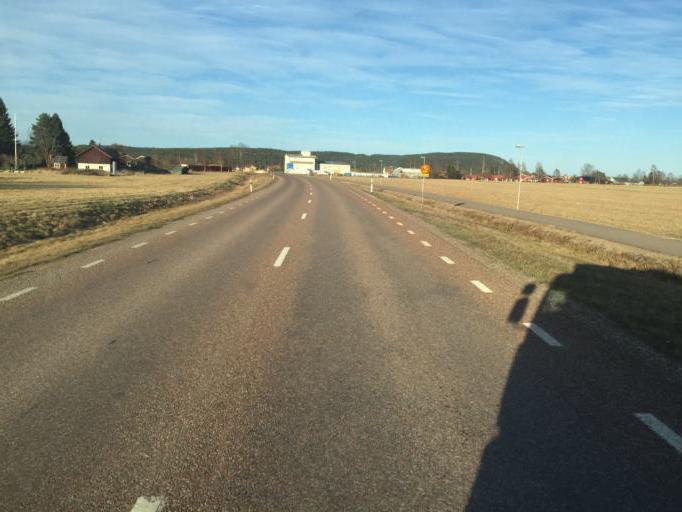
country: SE
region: Dalarna
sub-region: Gagnefs Kommun
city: Djuras
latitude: 60.5547
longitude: 15.1128
